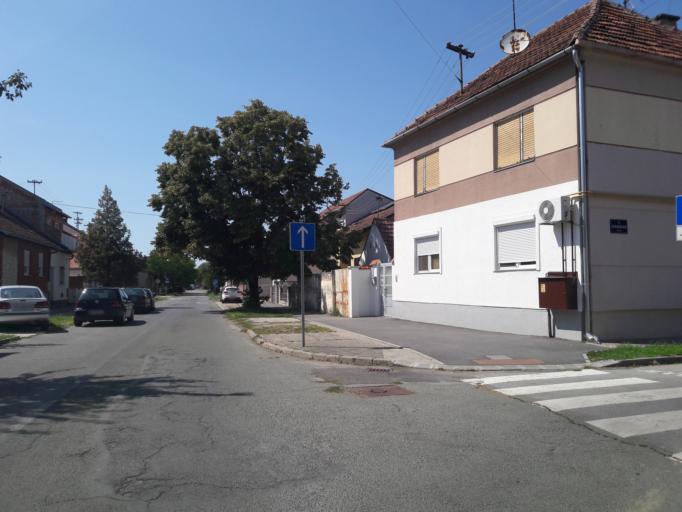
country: HR
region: Osjecko-Baranjska
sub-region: Grad Osijek
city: Osijek
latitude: 45.5581
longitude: 18.6559
